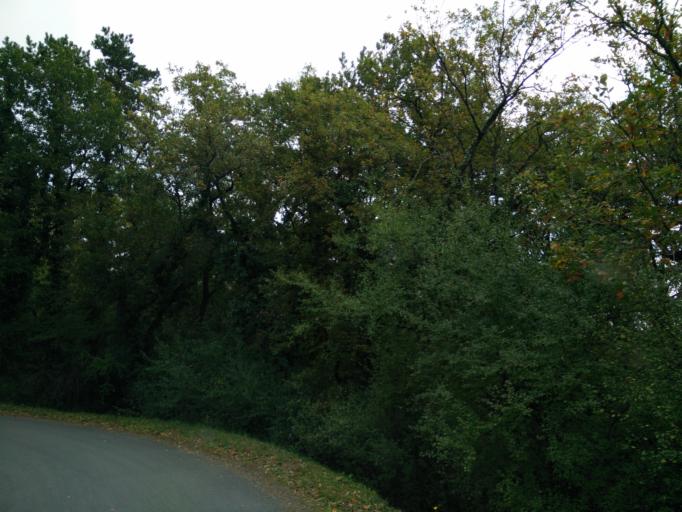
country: FR
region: Aquitaine
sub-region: Departement de la Dordogne
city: Montignac
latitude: 45.0526
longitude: 1.1665
